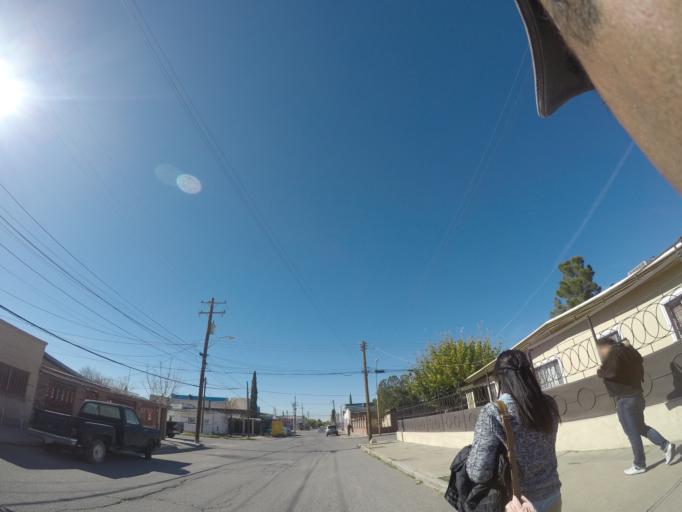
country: MX
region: Chihuahua
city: Ciudad Juarez
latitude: 31.7420
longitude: -106.4563
